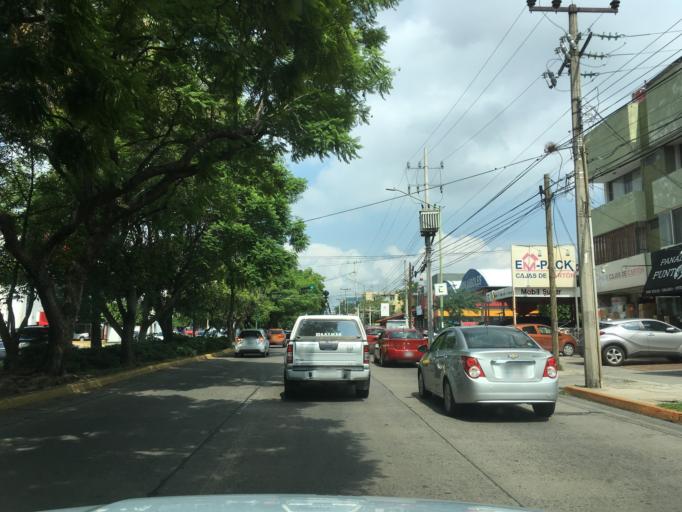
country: MX
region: Jalisco
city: Guadalajara
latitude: 20.6666
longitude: -103.3880
